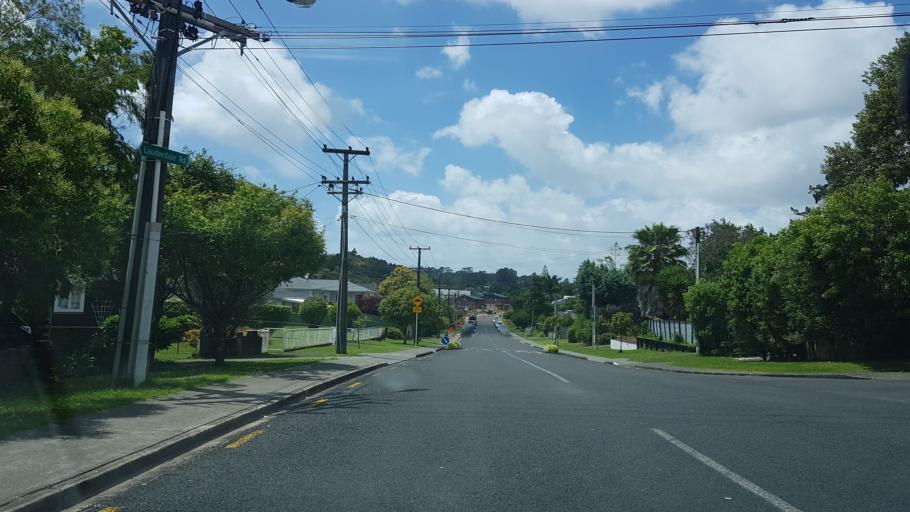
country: NZ
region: Auckland
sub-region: Auckland
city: North Shore
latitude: -36.7910
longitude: 174.7044
